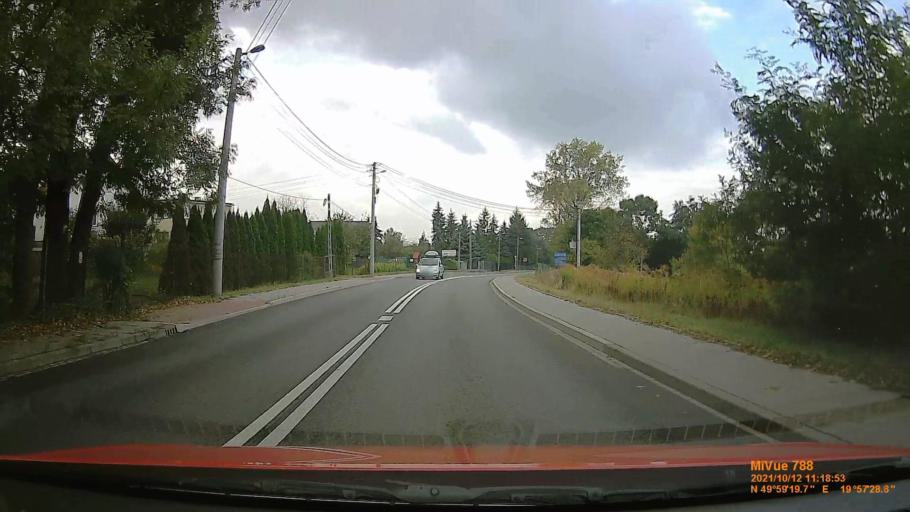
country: PL
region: Lesser Poland Voivodeship
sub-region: Powiat krakowski
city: Wrzasowice
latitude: 49.9888
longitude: 19.9578
